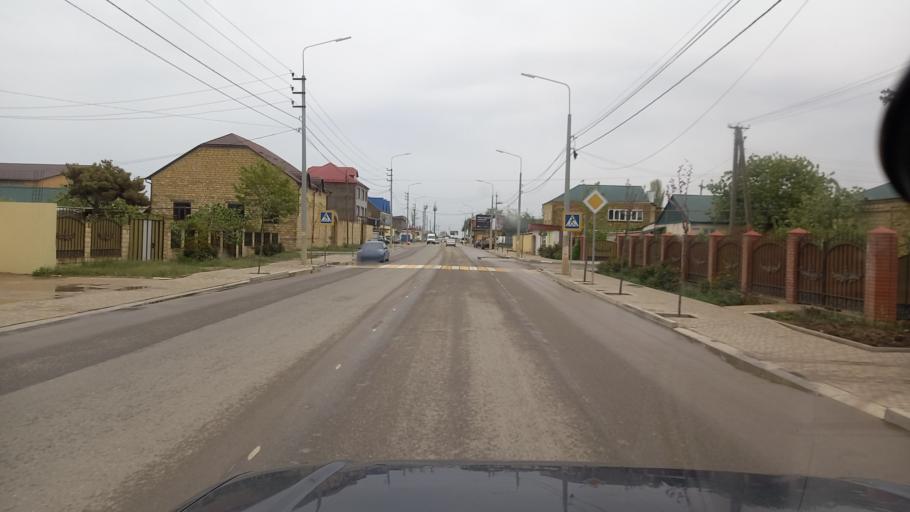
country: RU
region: Dagestan
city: Derbent
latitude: 42.0810
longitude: 48.2952
